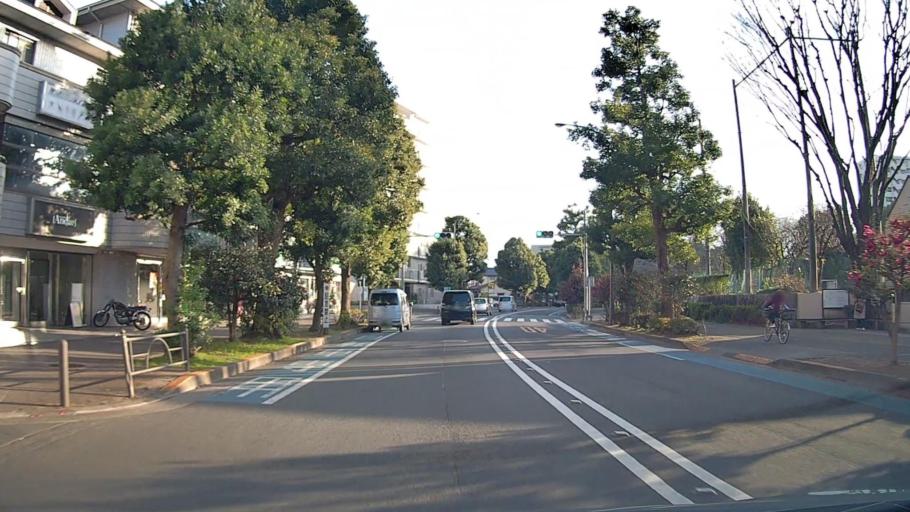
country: JP
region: Saitama
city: Wako
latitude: 35.7576
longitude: 139.6321
